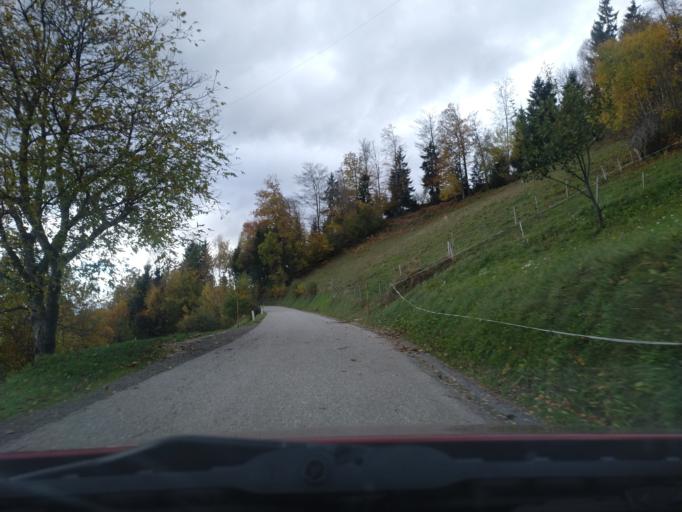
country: SI
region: Kamnik
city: Mekinje
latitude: 46.2652
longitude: 14.6856
